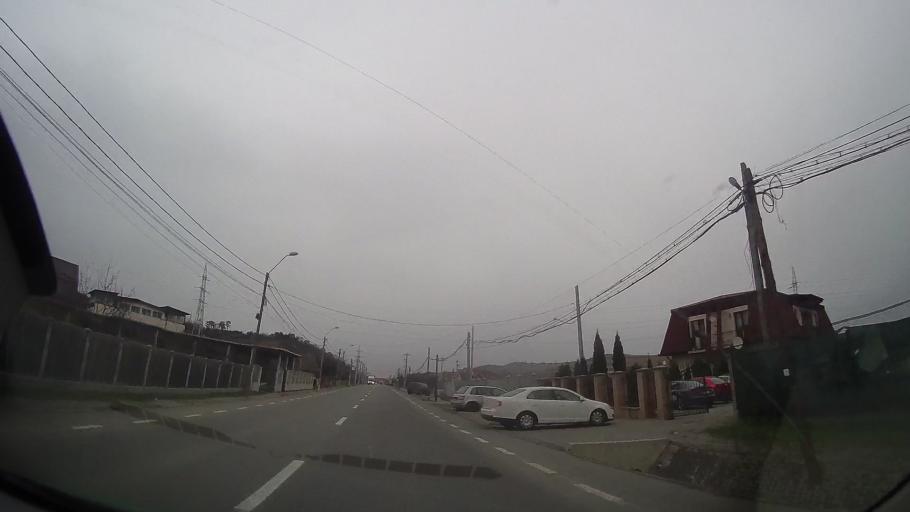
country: RO
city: Remetea
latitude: 46.5923
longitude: 24.5343
